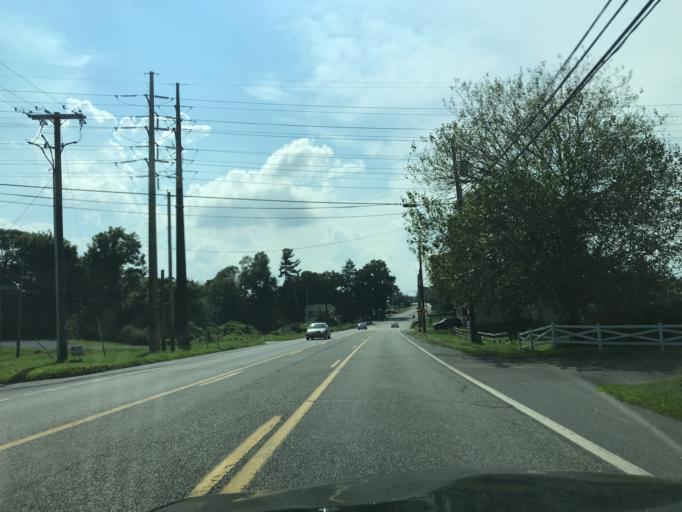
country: US
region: Pennsylvania
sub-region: Lancaster County
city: Columbia
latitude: 40.0320
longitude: -76.4684
